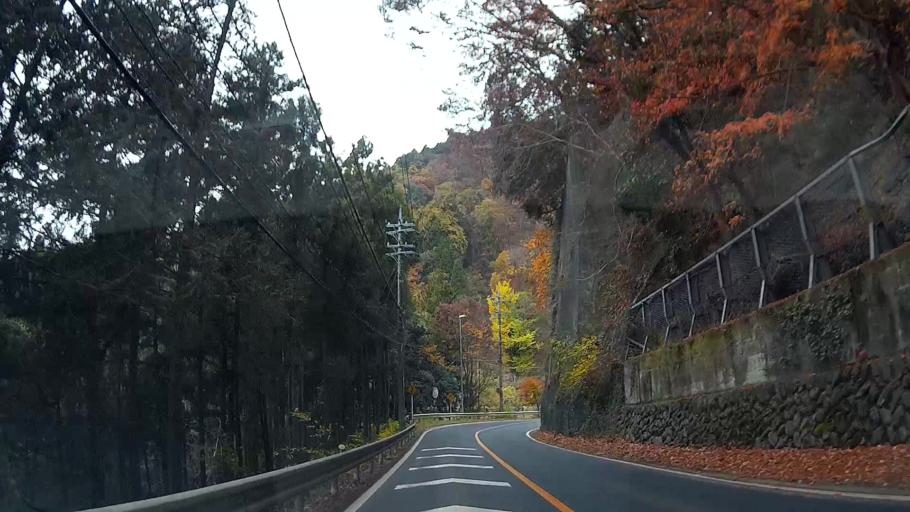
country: JP
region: Saitama
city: Chichibu
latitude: 35.9564
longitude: 138.9638
